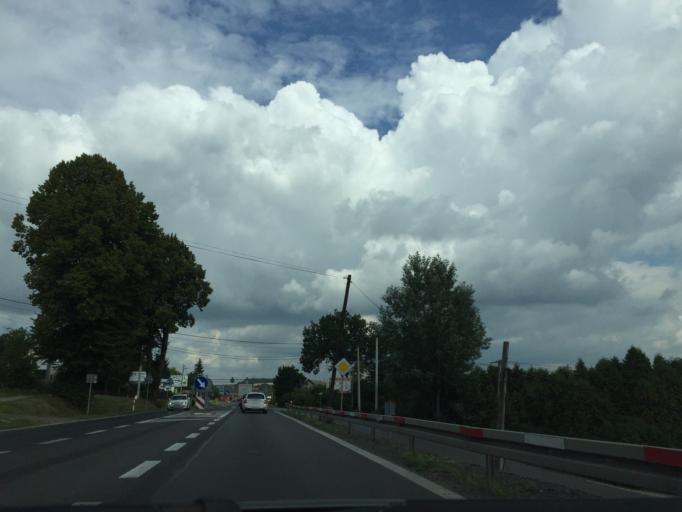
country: PL
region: Lesser Poland Voivodeship
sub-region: Powiat krakowski
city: Michalowice
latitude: 50.1499
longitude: 19.9837
